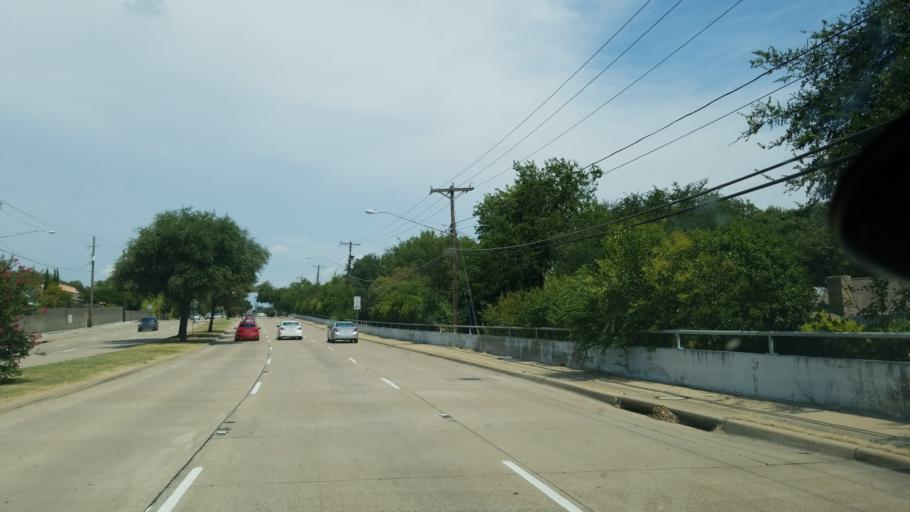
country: US
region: Texas
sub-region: Dallas County
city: Richardson
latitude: 32.9020
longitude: -96.7378
